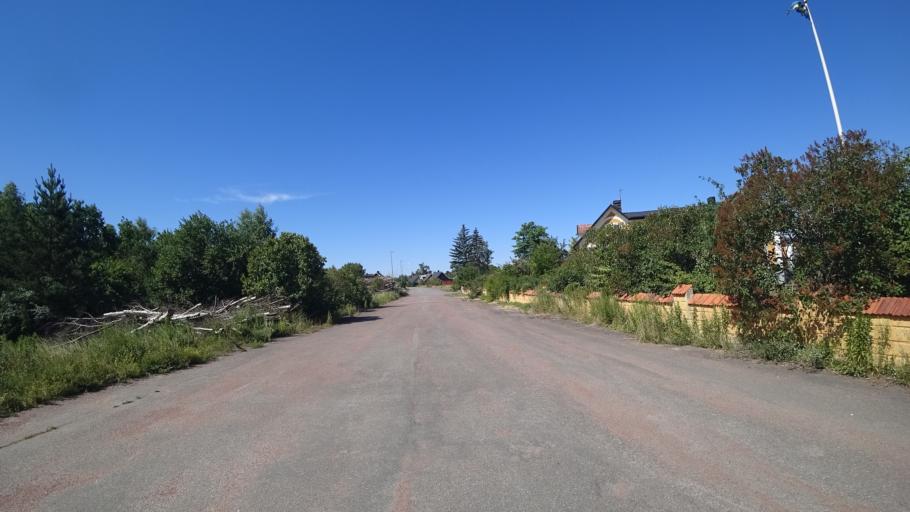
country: SE
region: Skane
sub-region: Kristianstads Kommun
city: Kristianstad
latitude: 56.0187
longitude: 14.1112
